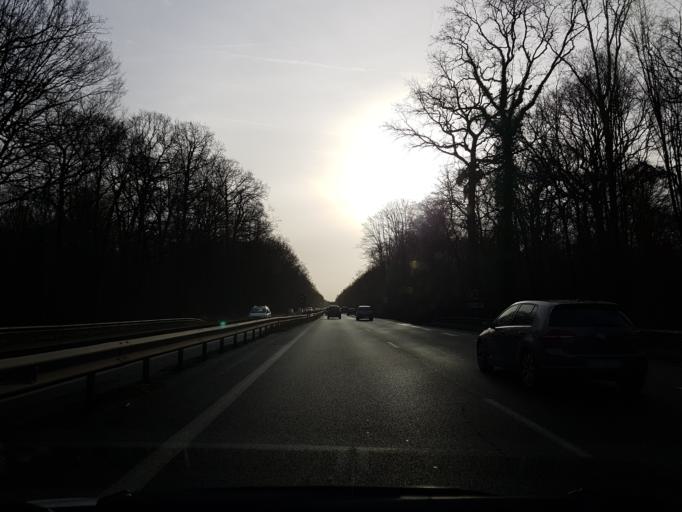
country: FR
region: Ile-de-France
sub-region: Departement de l'Essonne
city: Quincy-sous-Senart
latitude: 48.6566
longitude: 2.5225
